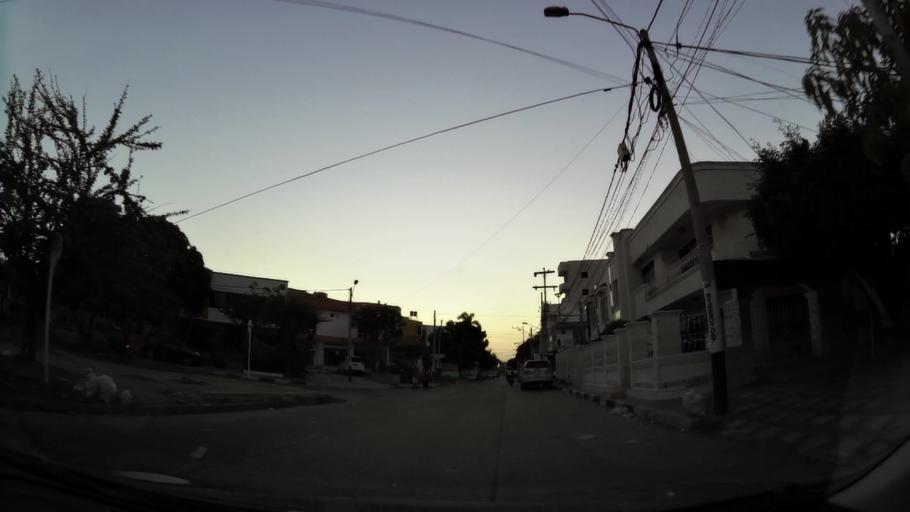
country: CO
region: Bolivar
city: Cartagena
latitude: 10.3884
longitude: -75.4893
